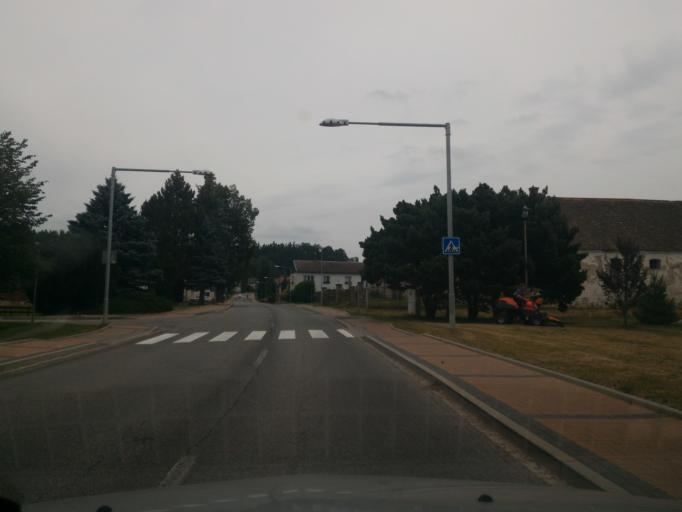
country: CZ
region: Vysocina
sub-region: Okres Jihlava
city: Telc
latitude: 49.1824
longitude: 15.4153
